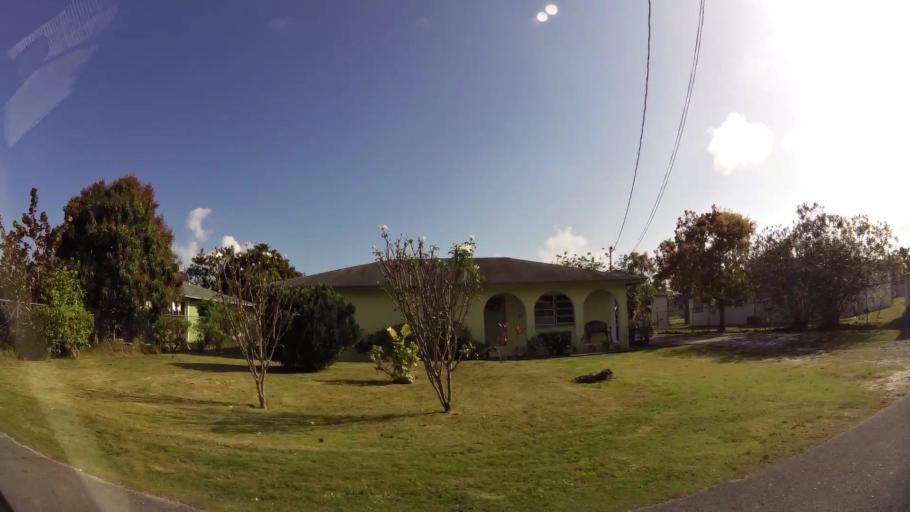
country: BS
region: Freeport
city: Lucaya
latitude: 26.5235
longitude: -78.6687
